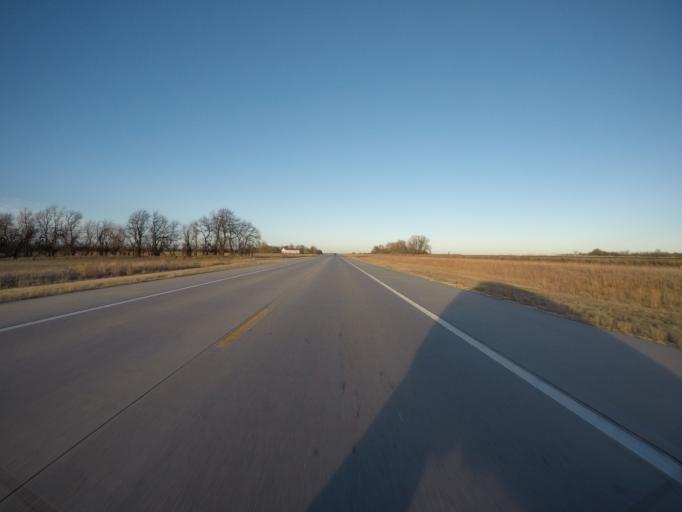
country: US
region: Kansas
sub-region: Harvey County
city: North Newton
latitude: 38.0817
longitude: -97.2934
